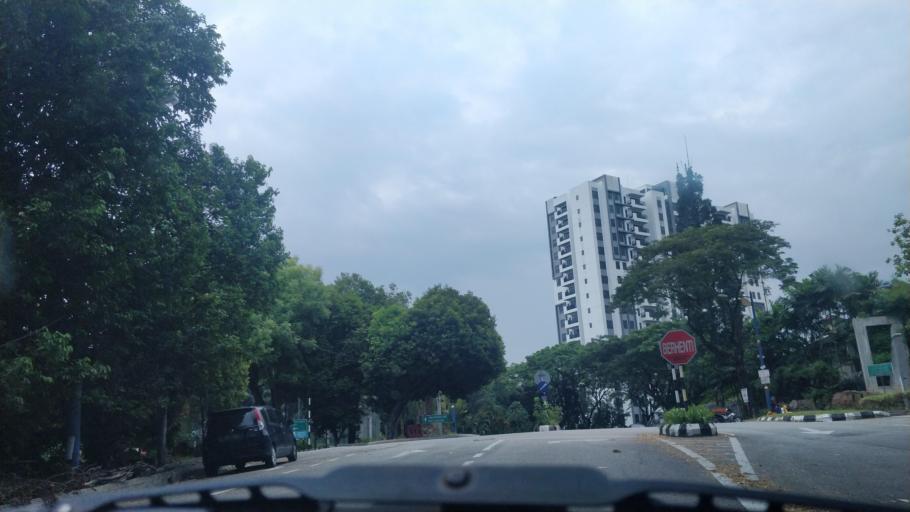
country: MY
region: Selangor
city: Kuang
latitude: 3.2084
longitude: 101.5814
